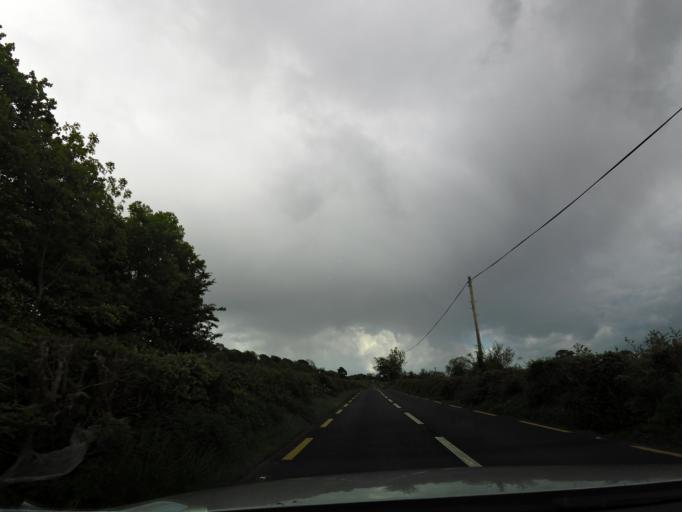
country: IE
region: Munster
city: Thurles
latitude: 52.7053
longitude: -7.8246
